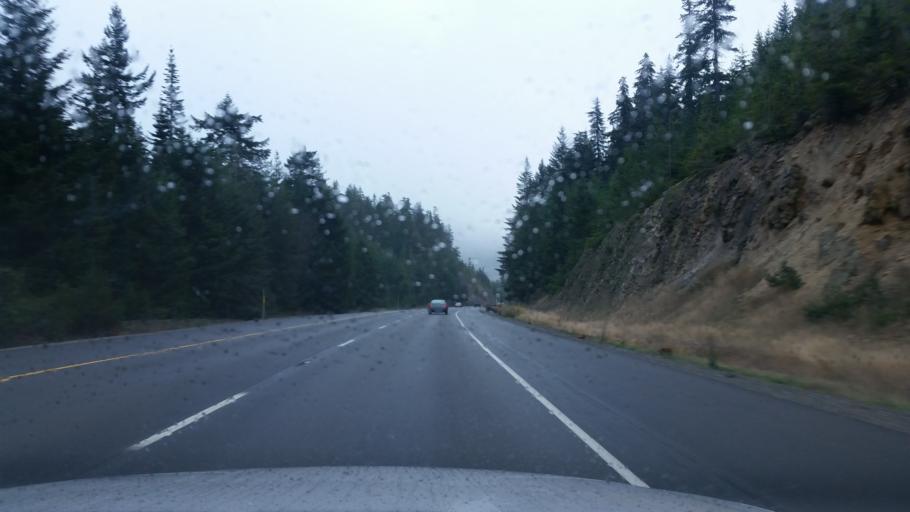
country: US
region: Washington
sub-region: Kittitas County
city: Cle Elum
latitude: 47.2680
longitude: -121.2379
